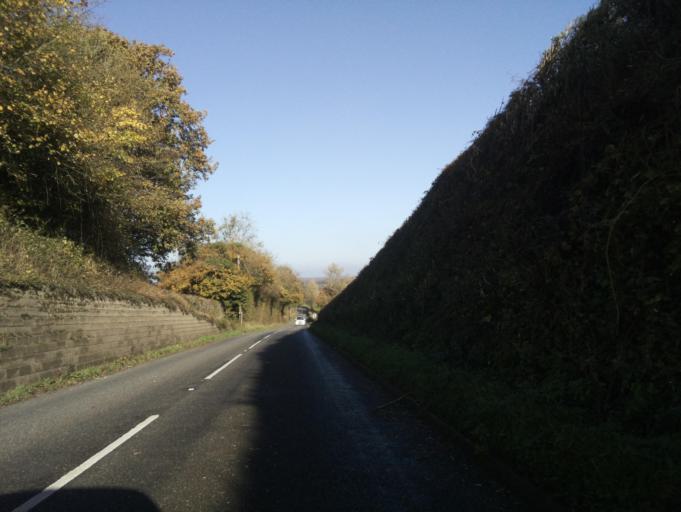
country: GB
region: England
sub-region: Somerset
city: Bruton
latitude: 51.1640
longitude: -2.4162
